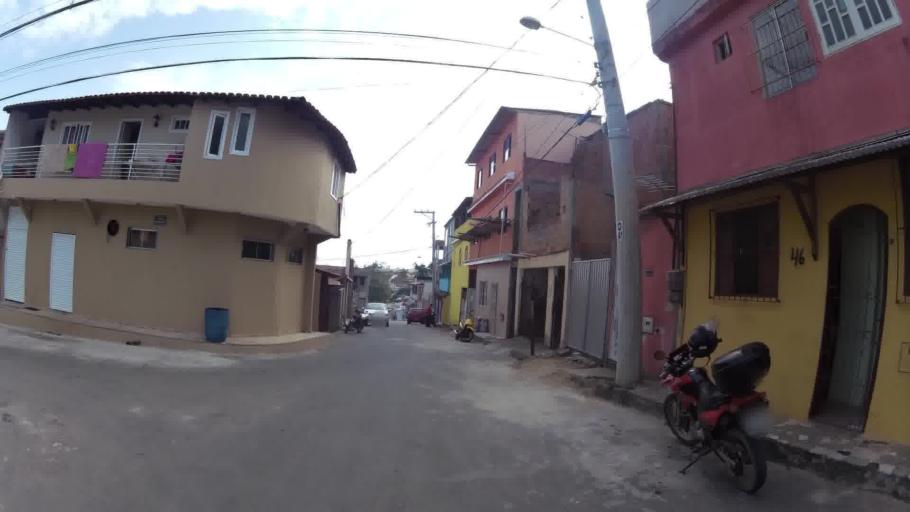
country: BR
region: Espirito Santo
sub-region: Itapemirim
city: Itapemirim
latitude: -21.0119
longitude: -40.8314
